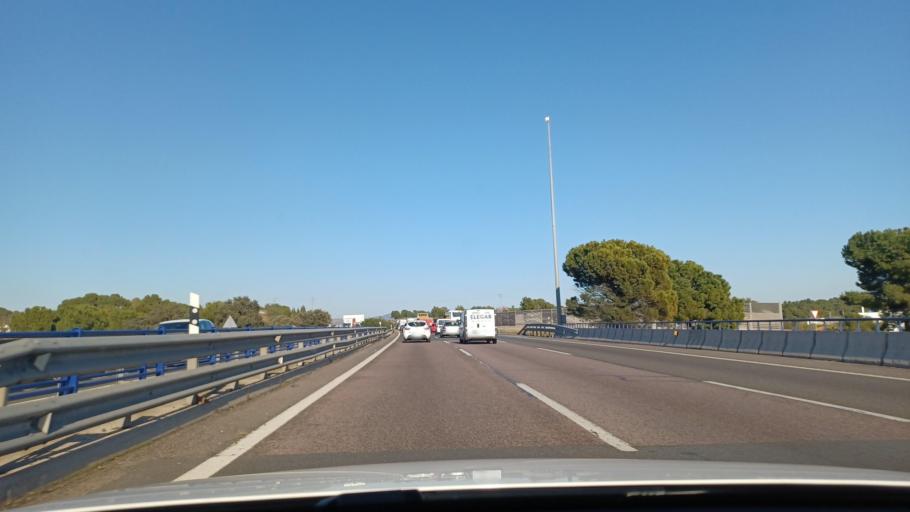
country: ES
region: Valencia
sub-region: Provincia de Valencia
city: Godella
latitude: 39.5577
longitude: -0.4315
